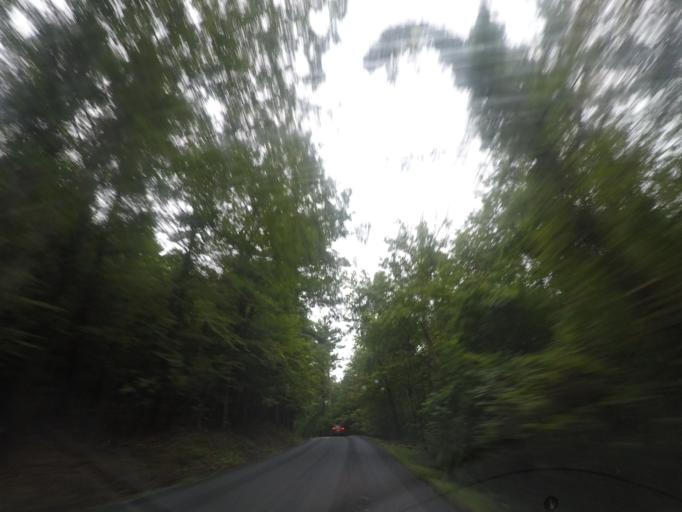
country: US
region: New York
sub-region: Rensselaer County
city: West Sand Lake
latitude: 42.6061
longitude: -73.6444
